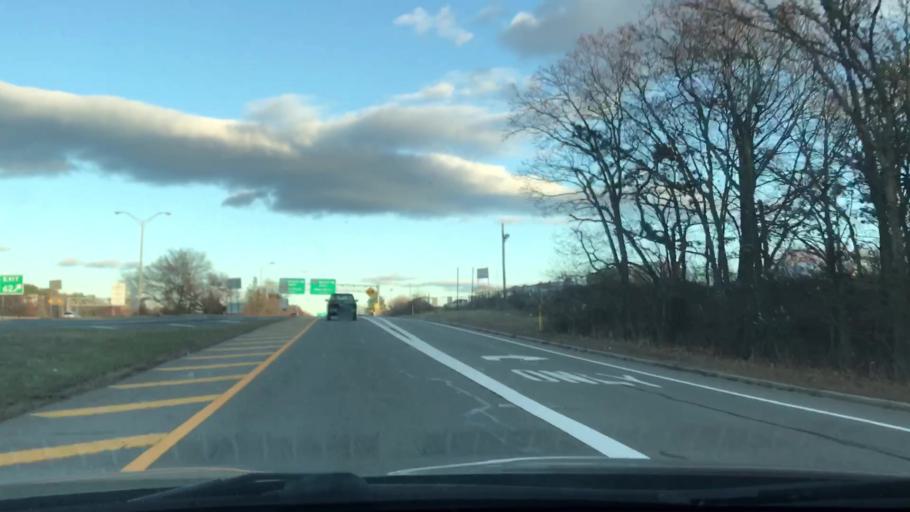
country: US
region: New York
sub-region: Suffolk County
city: Holtsville
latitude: 40.8184
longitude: -73.0621
